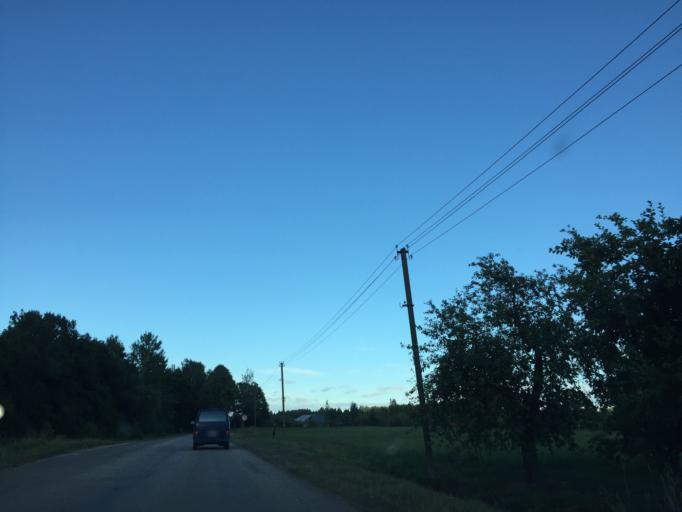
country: LV
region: Plavinu
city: Plavinas
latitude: 56.6100
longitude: 25.8096
